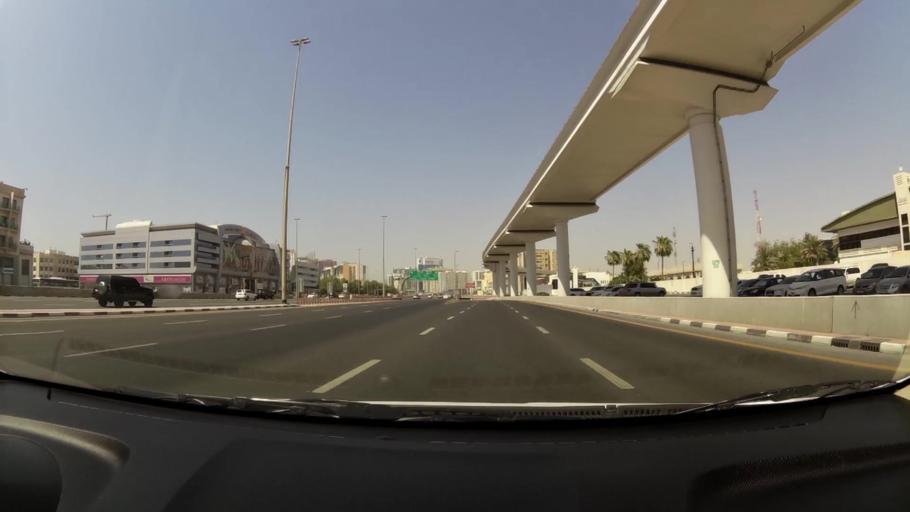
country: AE
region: Ash Shariqah
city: Sharjah
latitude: 25.2784
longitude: 55.3533
